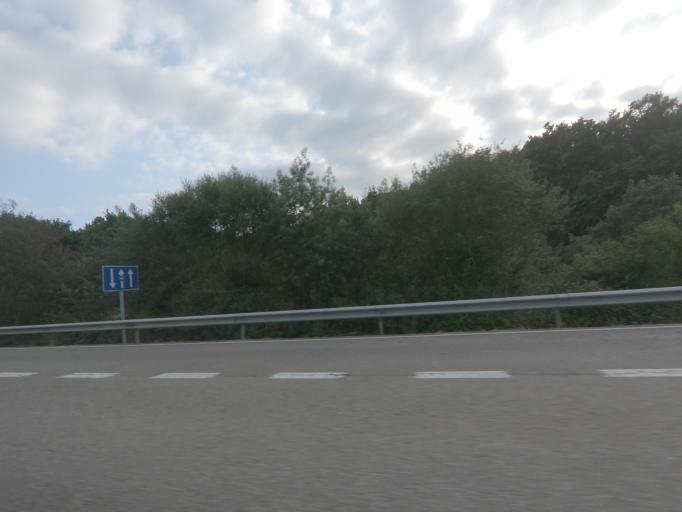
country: ES
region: Galicia
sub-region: Provincia de Ourense
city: Taboadela
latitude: 42.2328
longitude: -7.8420
